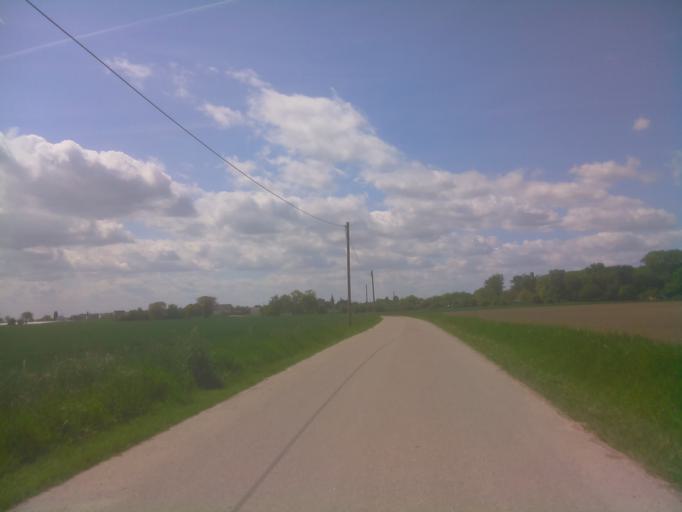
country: DE
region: Rheinland-Pfalz
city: Neuhofen
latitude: 49.4316
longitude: 8.4363
